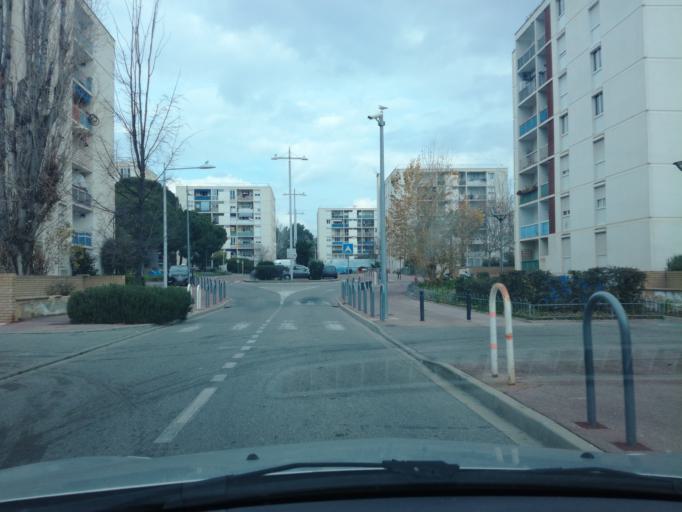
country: FR
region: Provence-Alpes-Cote d'Azur
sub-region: Departement des Alpes-Maritimes
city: Mandelieu-la-Napoule
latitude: 43.5559
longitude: 6.9632
